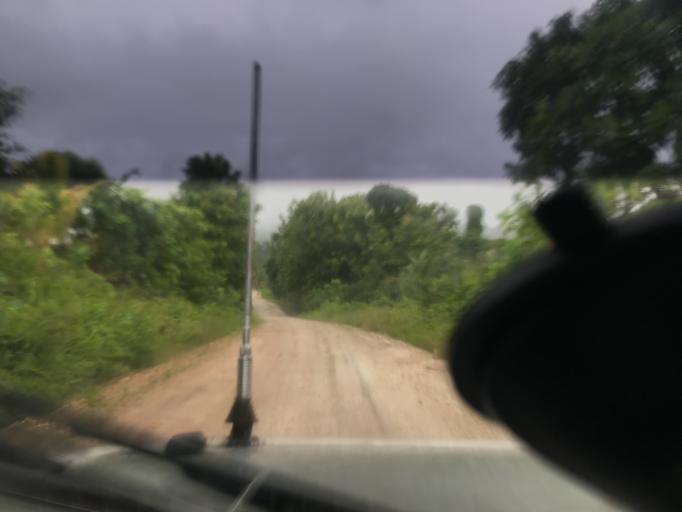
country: SB
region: Malaita
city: Auki
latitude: -9.0229
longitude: 160.8022
